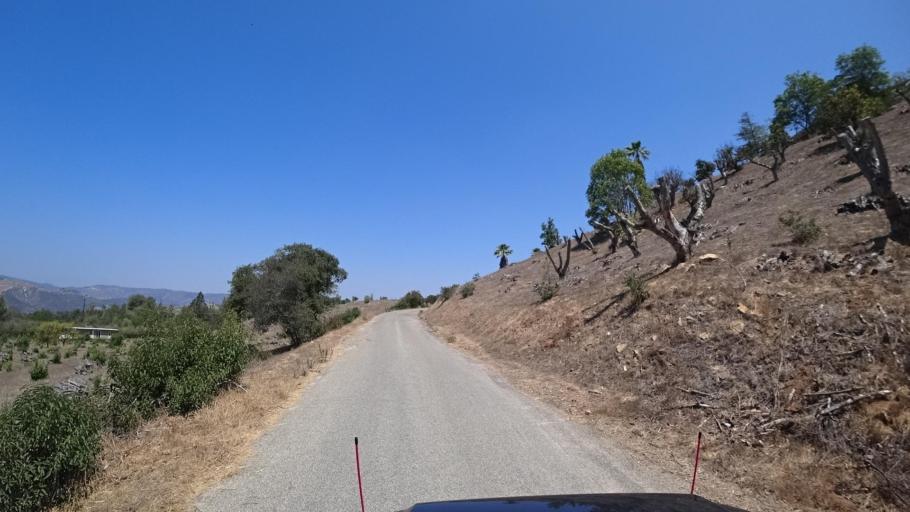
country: US
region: California
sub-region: San Diego County
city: Fallbrook
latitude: 33.4527
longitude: -117.2689
